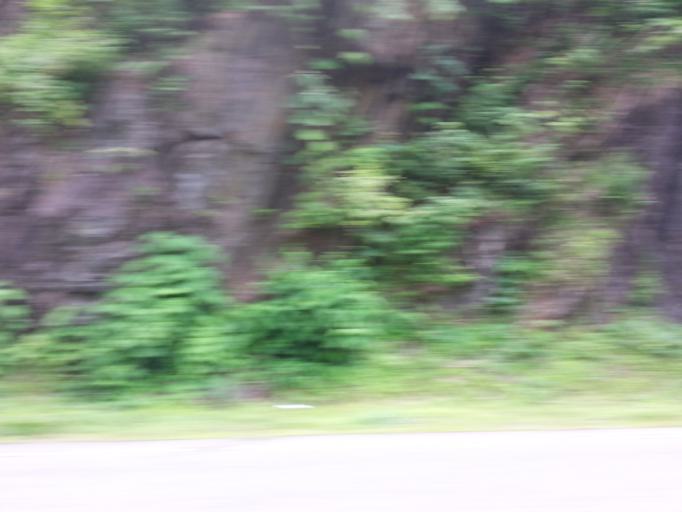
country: US
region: North Carolina
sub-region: Cherokee County
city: Andrews
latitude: 35.2296
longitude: -83.7380
